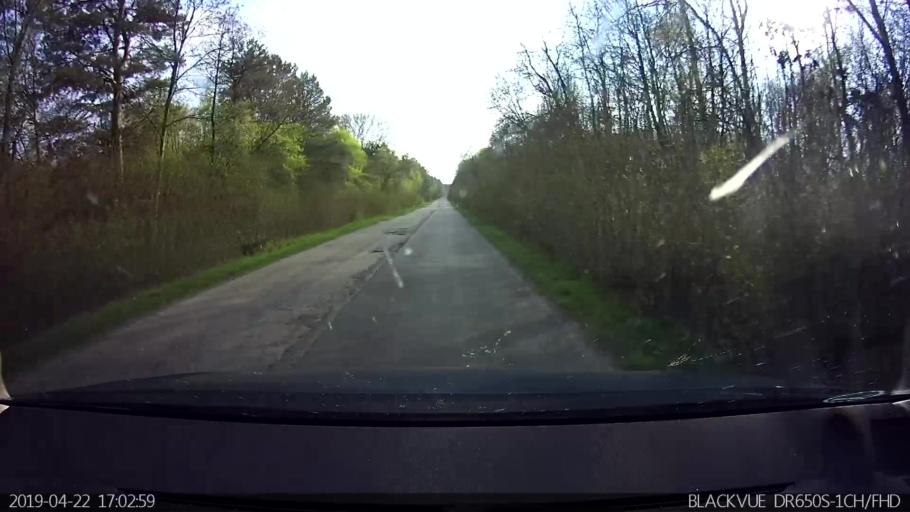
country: PL
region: Podlasie
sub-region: Powiat siemiatycki
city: Drohiczyn
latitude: 52.4212
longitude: 22.6968
